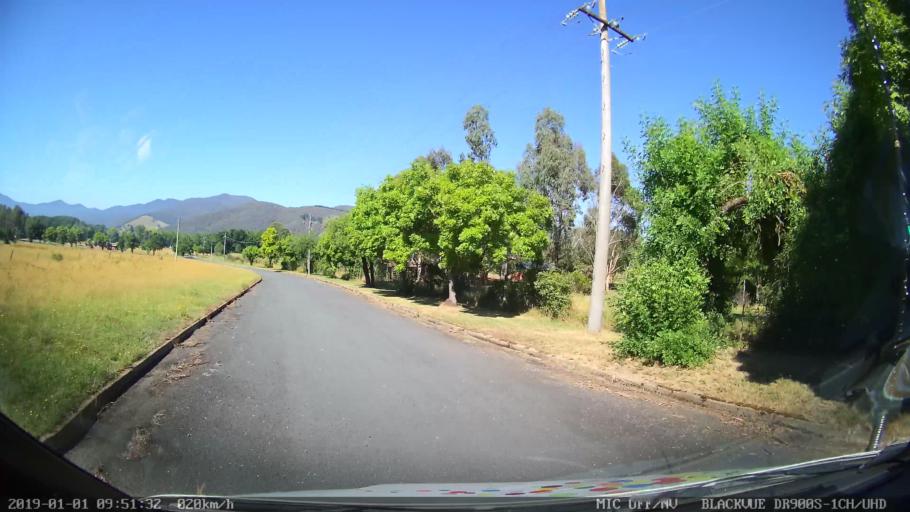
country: AU
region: New South Wales
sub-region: Snowy River
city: Jindabyne
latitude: -36.2148
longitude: 148.1237
